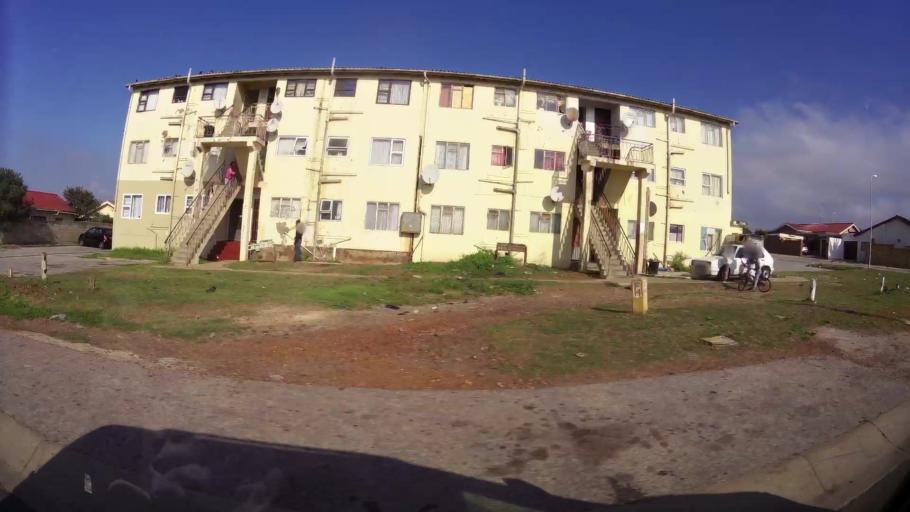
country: ZA
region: Eastern Cape
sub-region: Nelson Mandela Bay Metropolitan Municipality
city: Port Elizabeth
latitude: -33.9227
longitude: 25.5401
